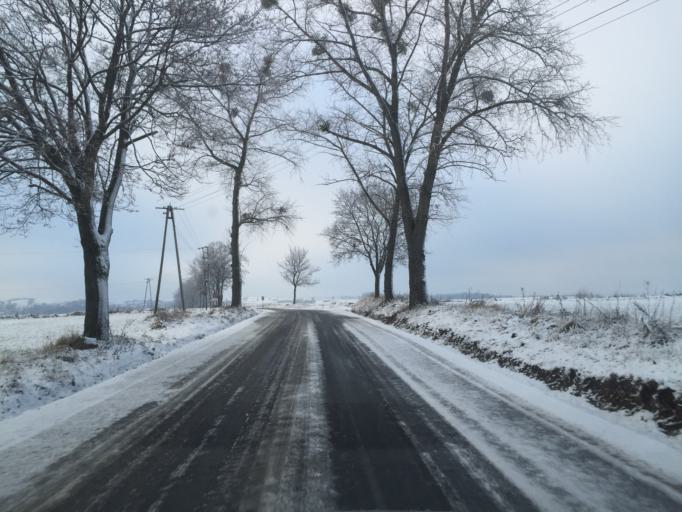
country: PL
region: Kujawsko-Pomorskie
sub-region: Powiat brodnicki
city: Bartniczka
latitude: 53.2528
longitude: 19.6579
